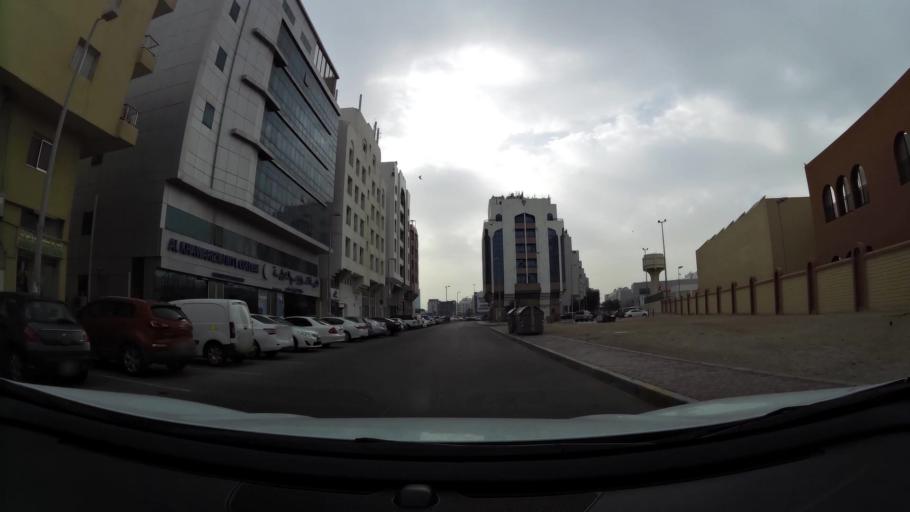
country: AE
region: Abu Dhabi
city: Abu Dhabi
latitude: 24.4686
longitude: 54.3792
